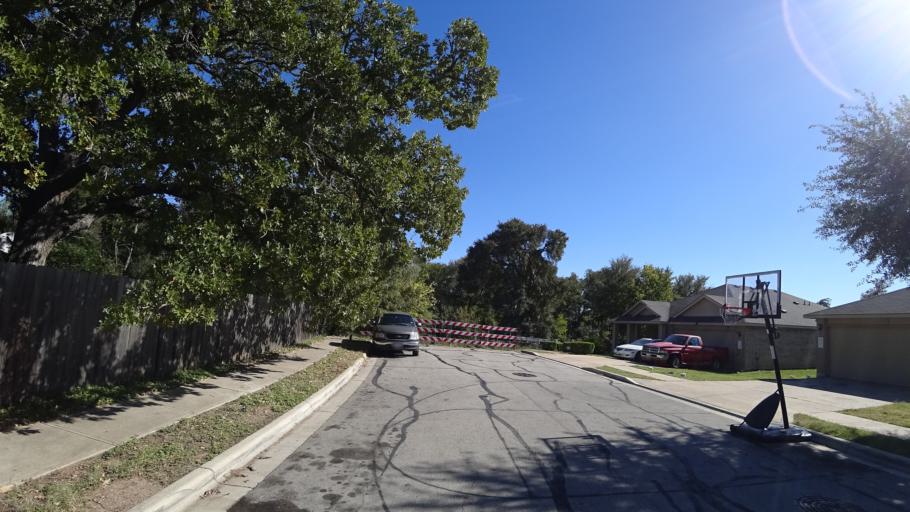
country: US
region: Texas
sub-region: Travis County
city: Hornsby Bend
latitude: 30.2821
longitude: -97.6272
